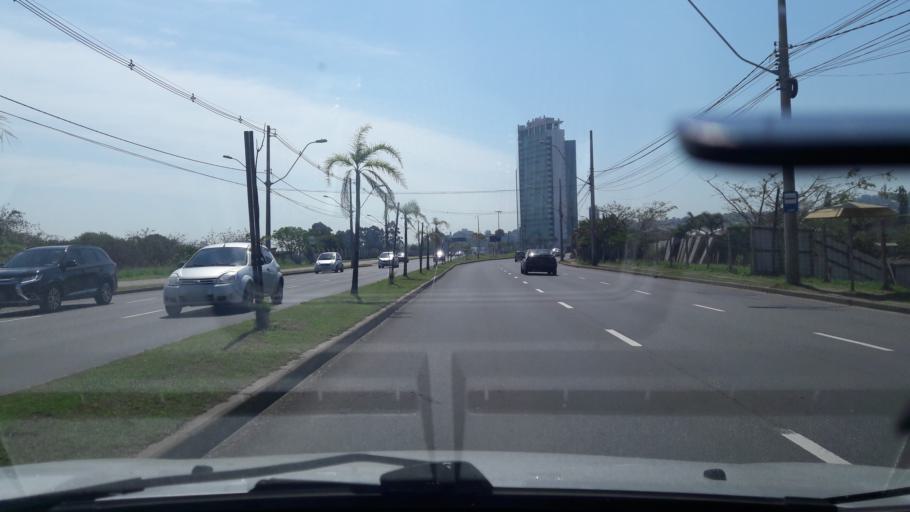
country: BR
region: Rio Grande do Sul
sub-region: Porto Alegre
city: Porto Alegre
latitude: -30.0907
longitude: -51.2488
